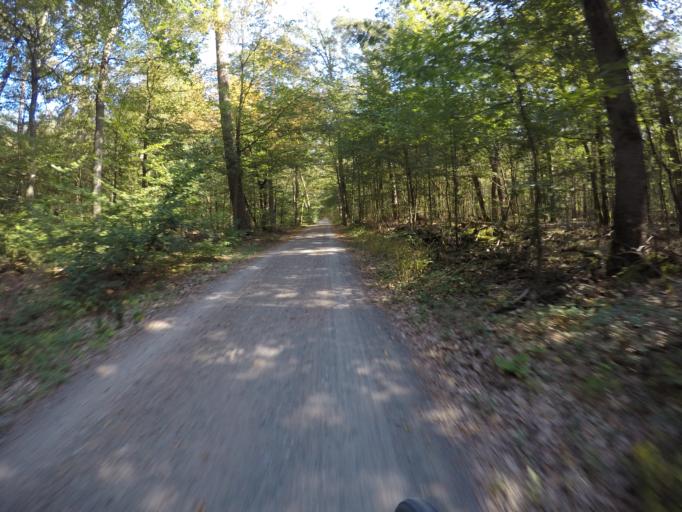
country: DE
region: Hesse
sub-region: Regierungsbezirk Darmstadt
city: Neu Isenburg
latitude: 50.0568
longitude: 8.6570
